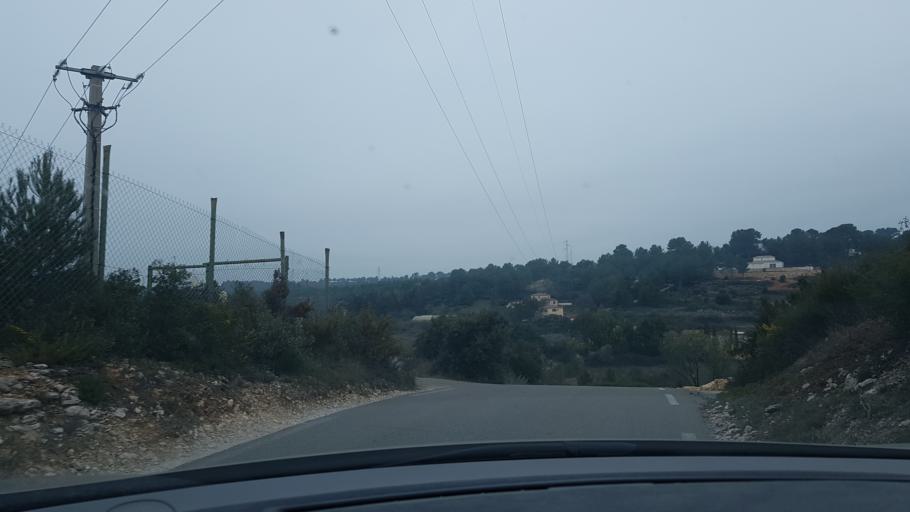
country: FR
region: Provence-Alpes-Cote d'Azur
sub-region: Departement des Bouches-du-Rhone
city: Meyreuil
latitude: 43.4810
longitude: 5.4823
